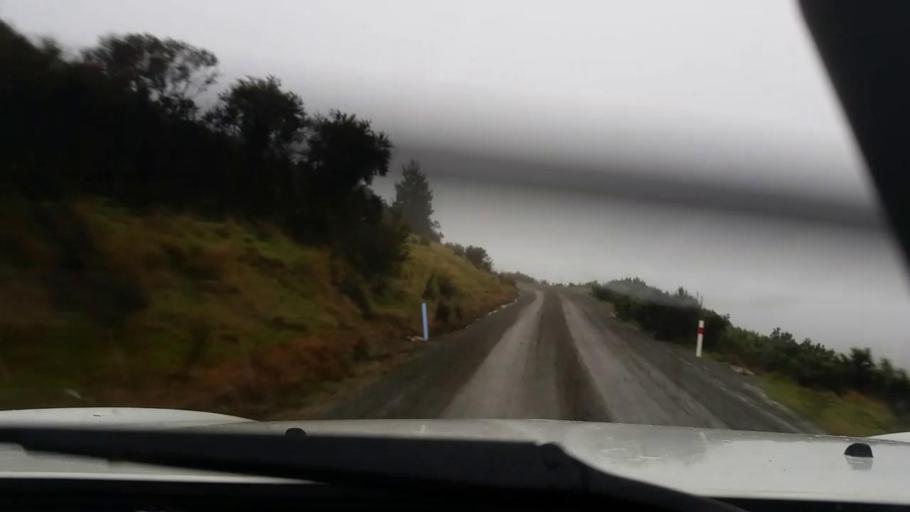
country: NZ
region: Wellington
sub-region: Masterton District
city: Masterton
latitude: -41.2461
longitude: 175.8780
